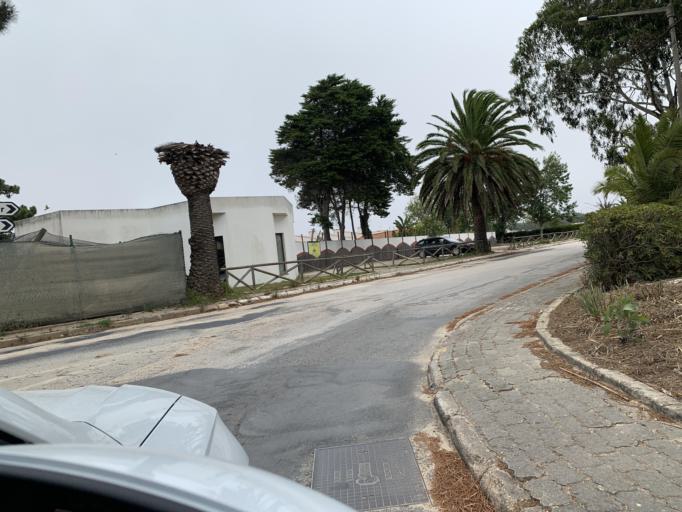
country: PT
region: Faro
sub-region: Aljezur
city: Aljezur
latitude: 37.3036
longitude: -8.8504
